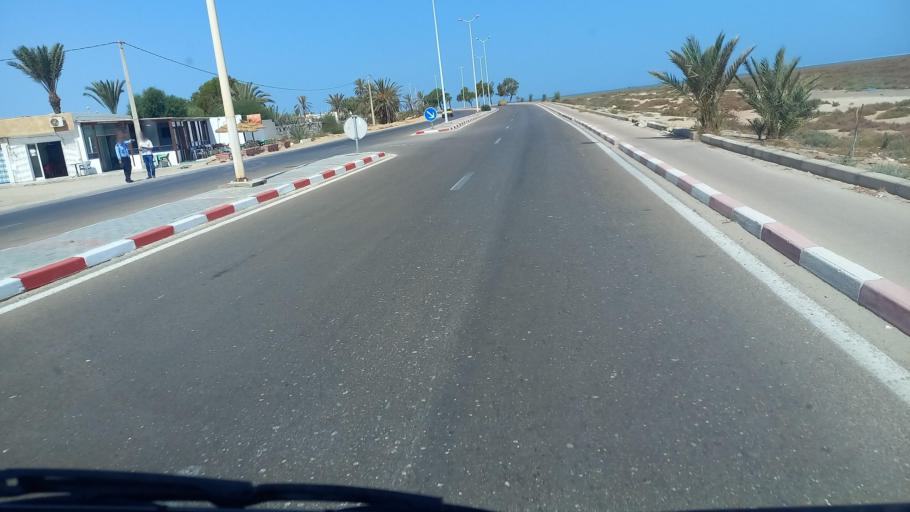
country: TN
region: Madanin
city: Houmt Souk
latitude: 33.8710
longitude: 10.9364
